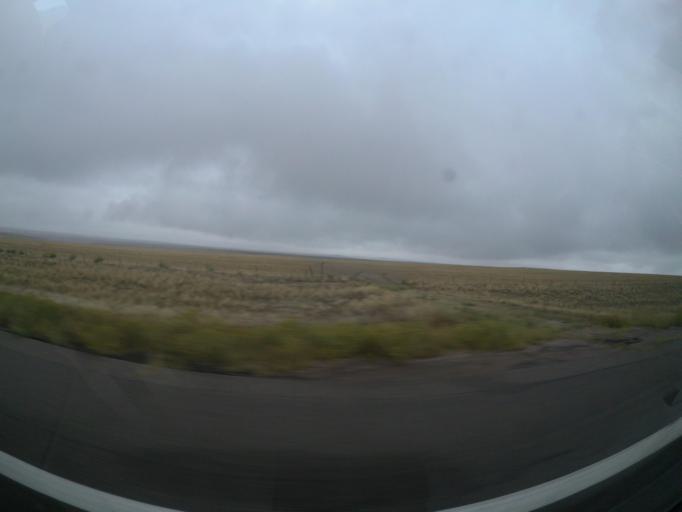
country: US
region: Colorado
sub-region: Arapahoe County
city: Byers
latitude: 39.7332
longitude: -103.8991
